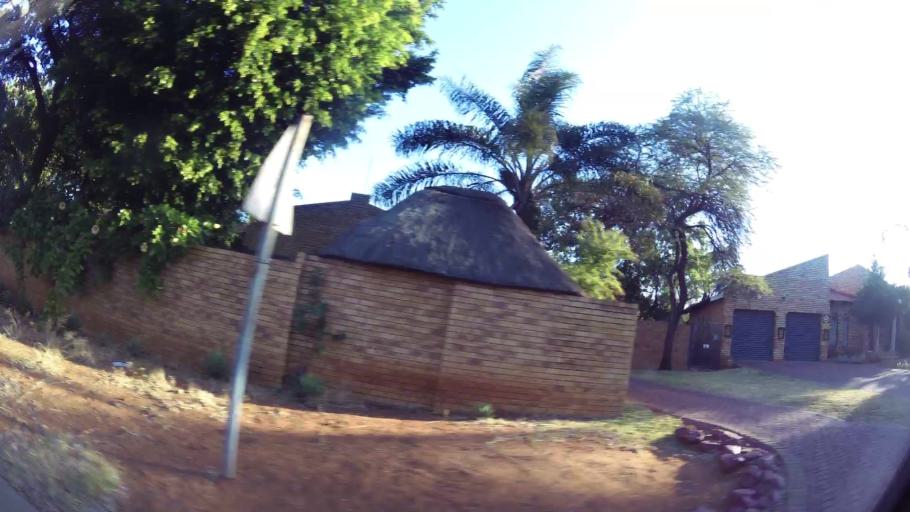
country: ZA
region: North-West
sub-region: Bojanala Platinum District Municipality
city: Rustenburg
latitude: -25.6845
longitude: 27.2053
